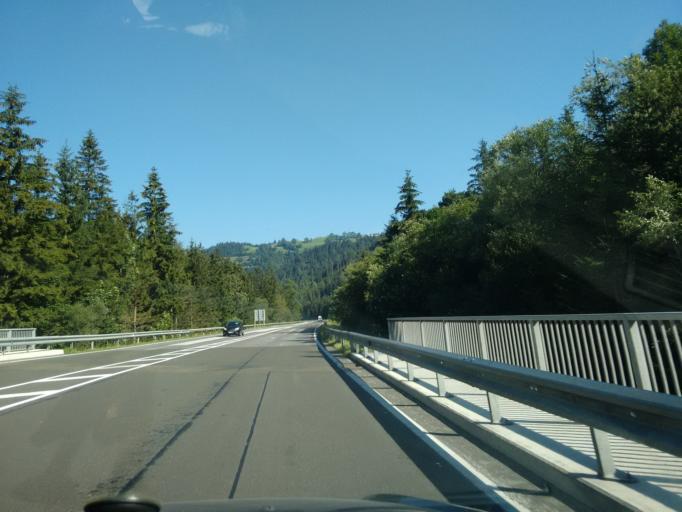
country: AT
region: Styria
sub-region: Politischer Bezirk Liezen
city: Tauplitz
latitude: 47.5365
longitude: 14.0496
